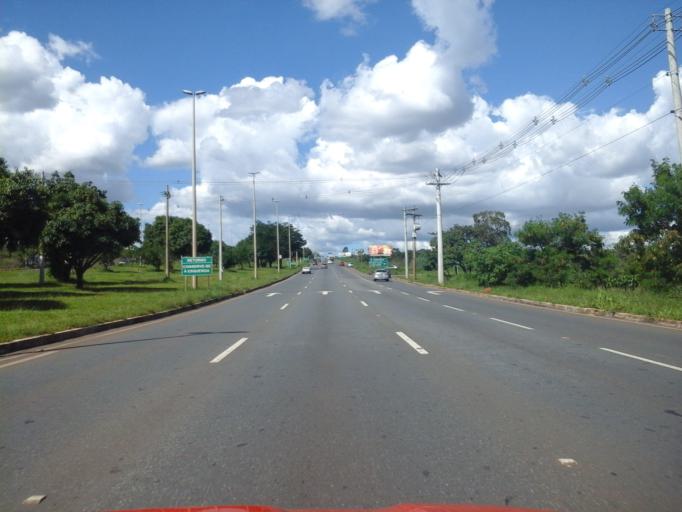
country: BR
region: Federal District
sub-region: Brasilia
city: Brasilia
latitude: -15.7256
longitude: -47.9076
